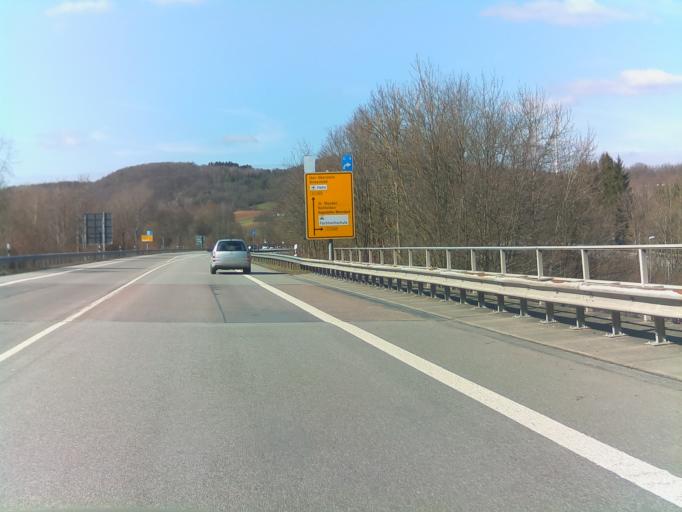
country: DE
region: Rheinland-Pfalz
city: Ellweiler
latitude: 49.6030
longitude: 7.1656
